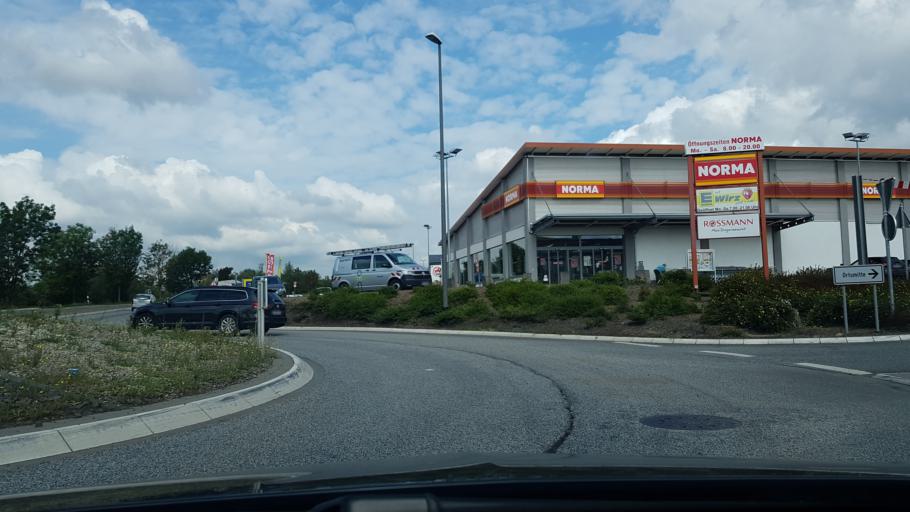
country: DE
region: Rheinland-Pfalz
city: Plaidt
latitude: 50.3879
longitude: 7.3832
